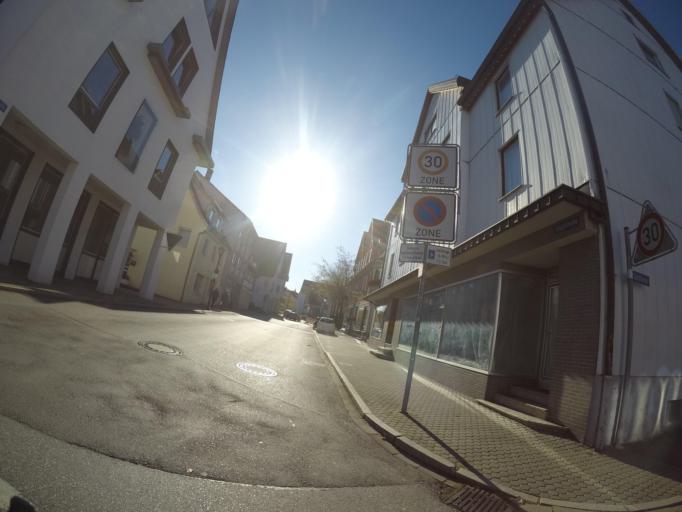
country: DE
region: Baden-Wuerttemberg
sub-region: Tuebingen Region
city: Saulgau
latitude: 48.0185
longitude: 9.4979
